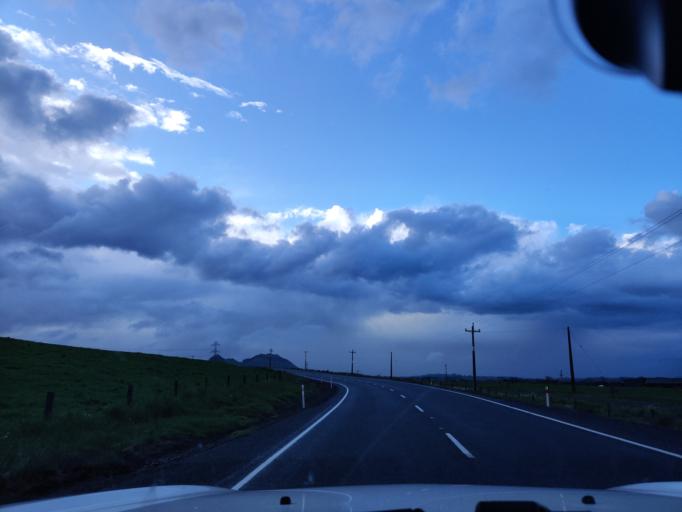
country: NZ
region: Waikato
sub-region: South Waikato District
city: Tokoroa
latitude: -38.3925
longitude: 175.7812
